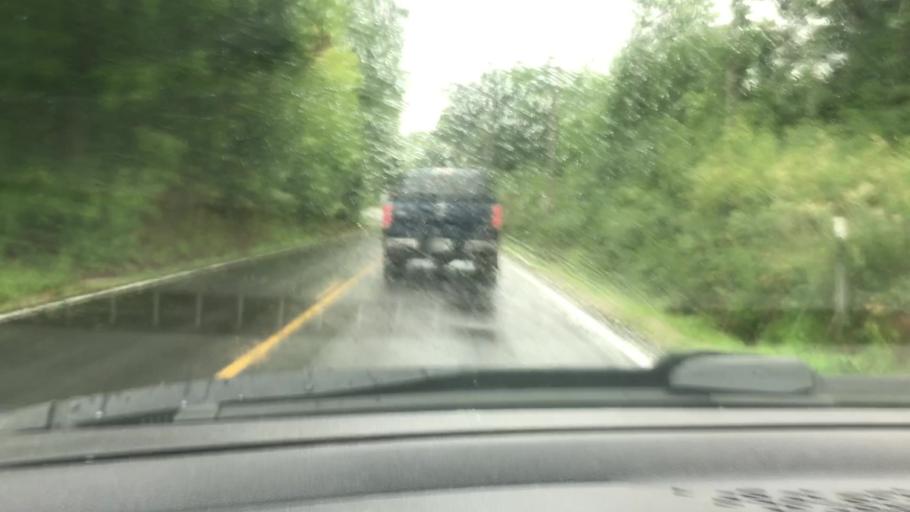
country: US
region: New Hampshire
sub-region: Rockingham County
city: Candia
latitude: 43.1590
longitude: -71.2411
